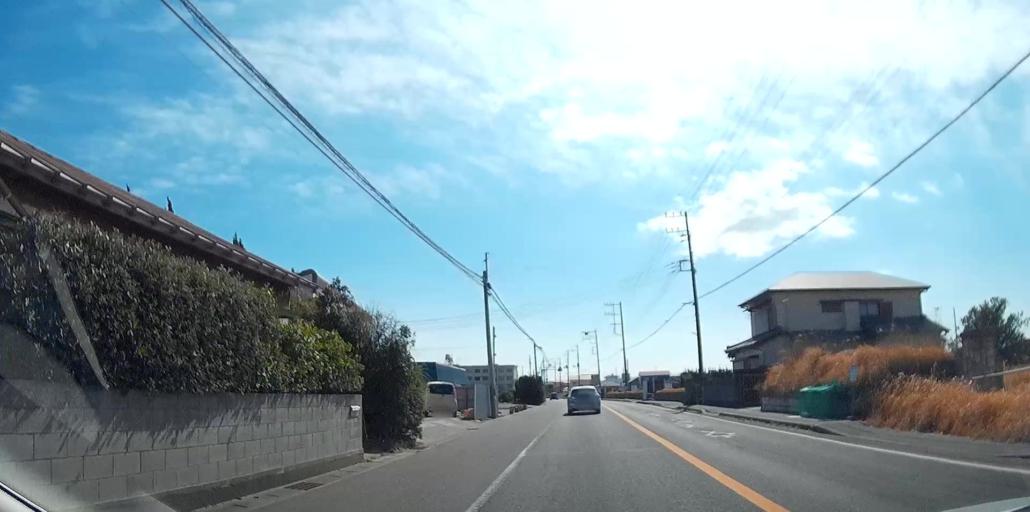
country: JP
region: Chiba
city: Tateyama
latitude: 35.0219
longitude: 139.8552
